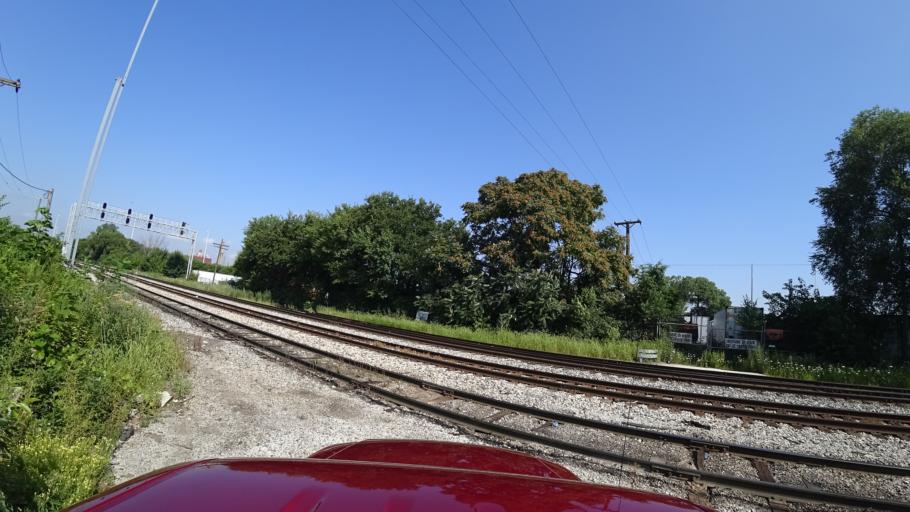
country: US
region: Illinois
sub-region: Cook County
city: Cicero
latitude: 41.8261
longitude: -87.7094
